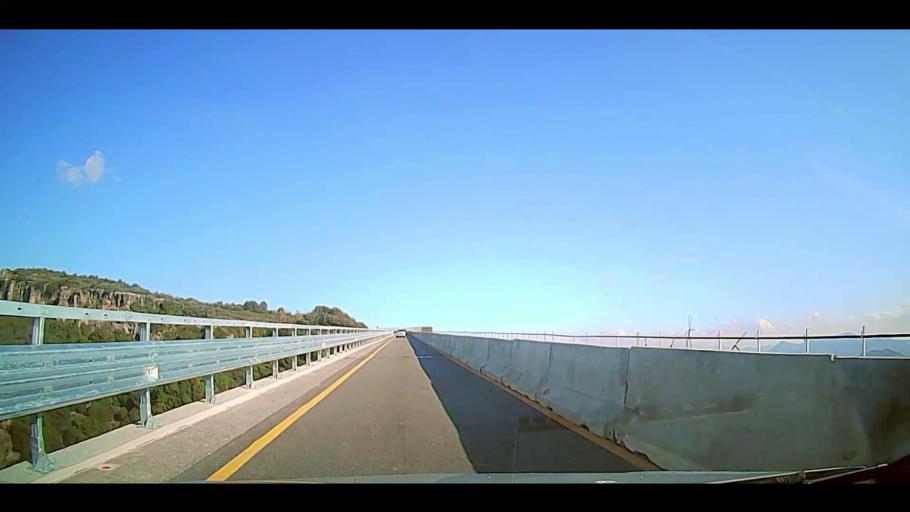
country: IT
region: Calabria
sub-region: Provincia di Crotone
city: Caccuri
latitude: 39.2236
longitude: 16.7943
